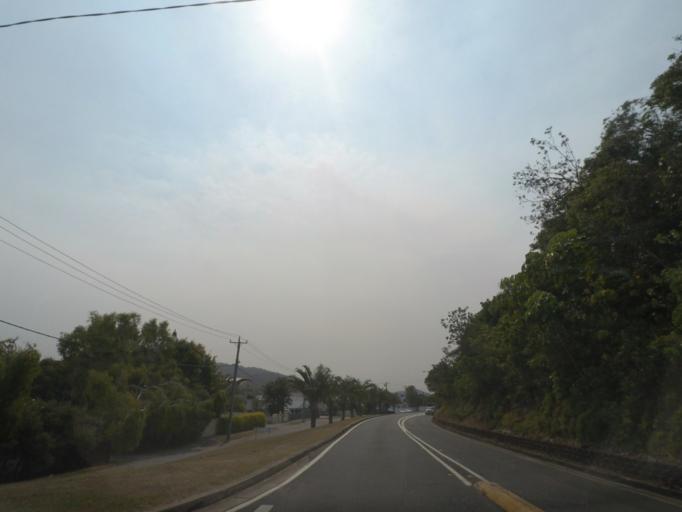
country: AU
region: New South Wales
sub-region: Tweed
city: Casuarina
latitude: -28.3344
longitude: 153.5723
